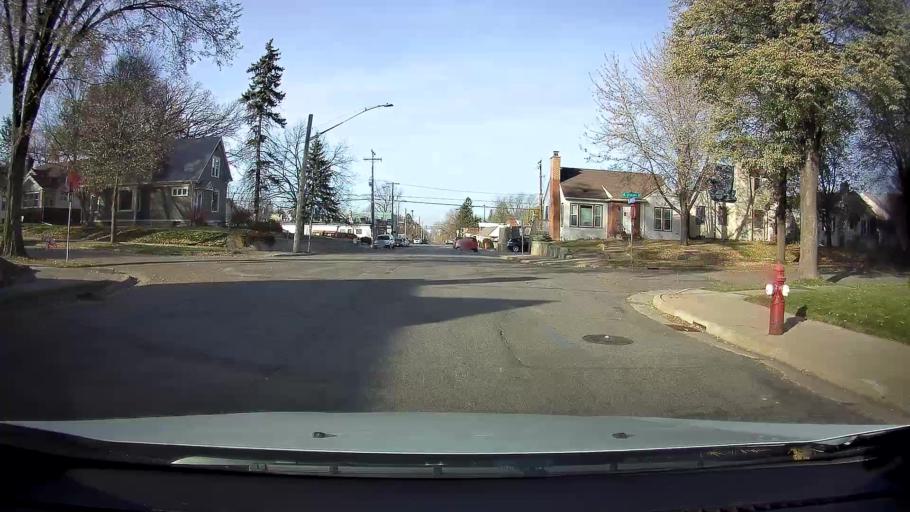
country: US
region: Minnesota
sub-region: Hennepin County
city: Saint Anthony
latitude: 45.0205
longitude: -93.2356
